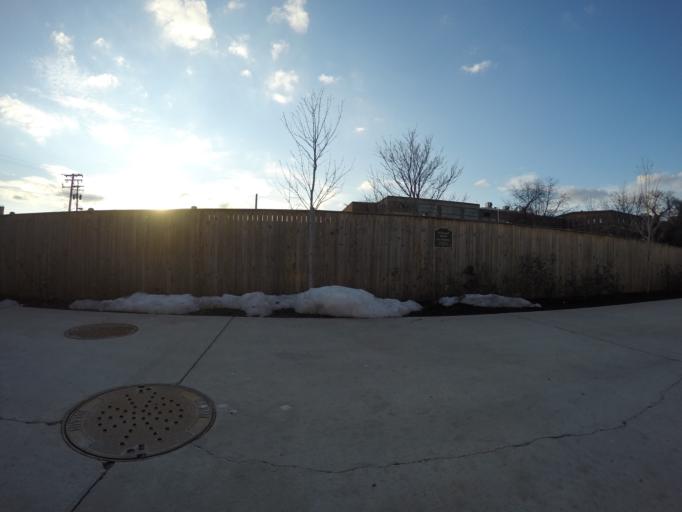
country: US
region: Maryland
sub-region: Baltimore County
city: Dundalk
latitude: 39.2841
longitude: -76.5582
